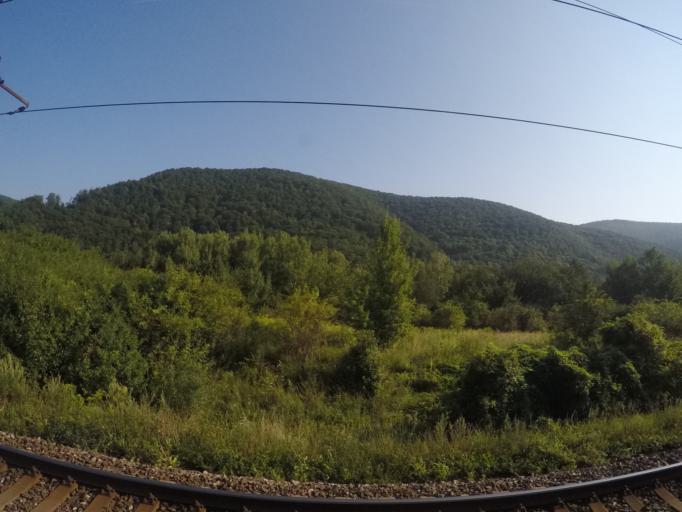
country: SK
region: Presovsky
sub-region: Okres Presov
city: Presov
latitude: 48.8783
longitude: 21.1209
